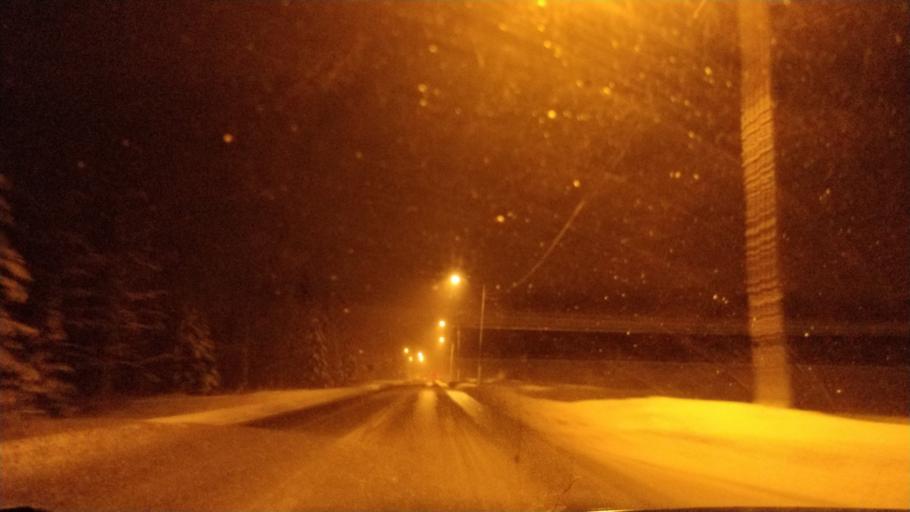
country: FI
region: Lapland
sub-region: Rovaniemi
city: Rovaniemi
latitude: 66.2785
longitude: 25.3336
